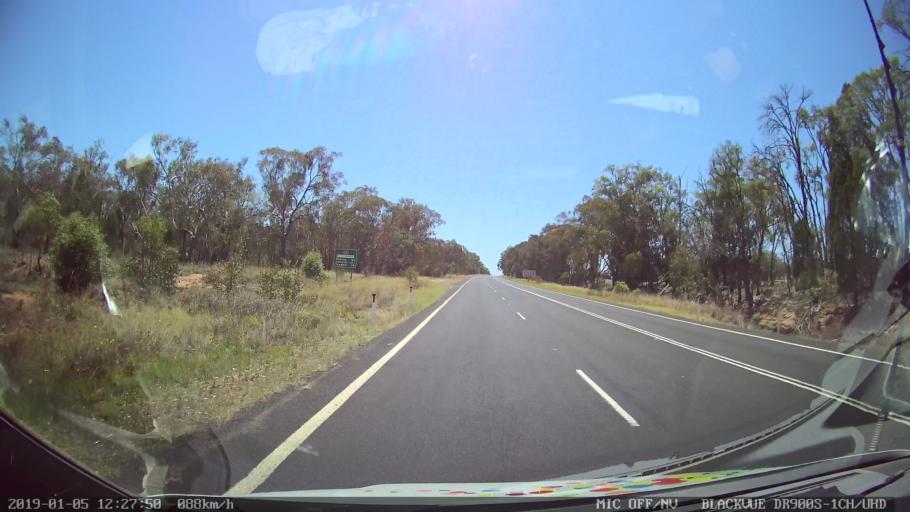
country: AU
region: New South Wales
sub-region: Warrumbungle Shire
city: Coonabarabran
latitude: -31.2448
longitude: 149.3148
